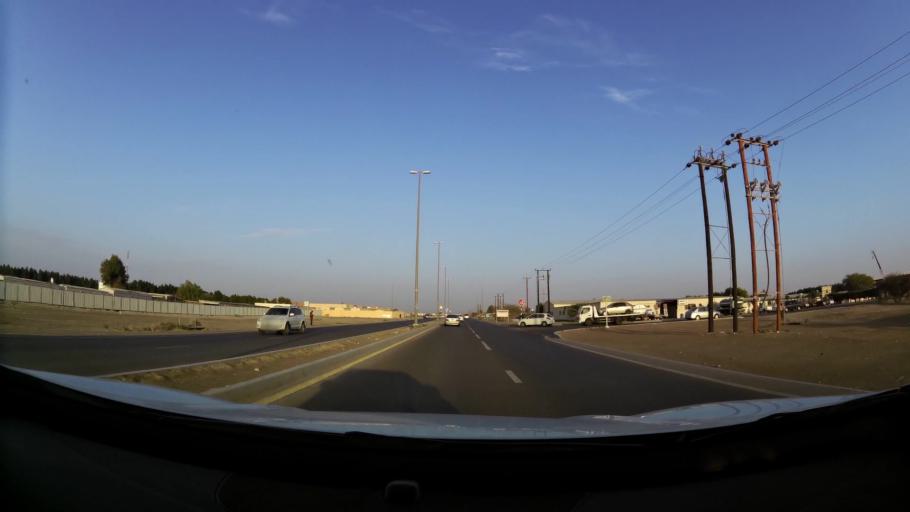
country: AE
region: Abu Dhabi
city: Al Ain
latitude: 24.1589
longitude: 55.8152
